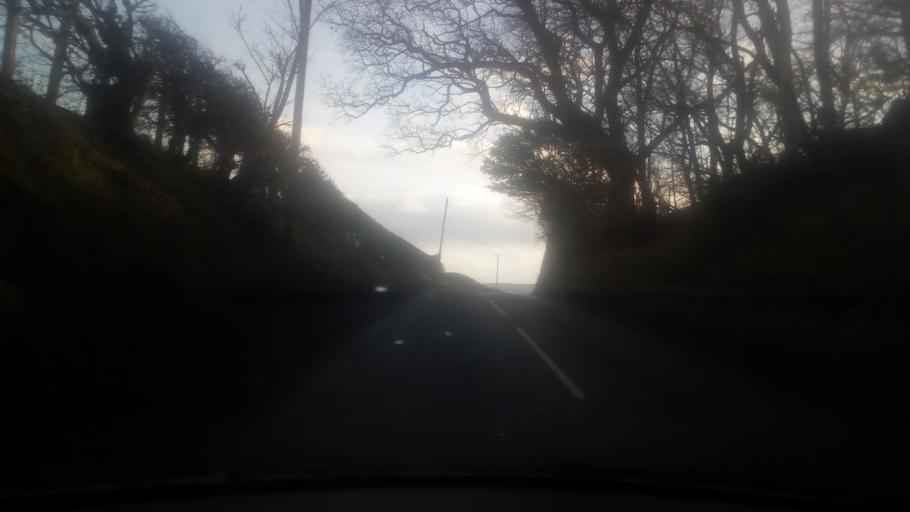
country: GB
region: Scotland
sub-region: The Scottish Borders
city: Kelso
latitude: 55.6604
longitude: -2.3834
